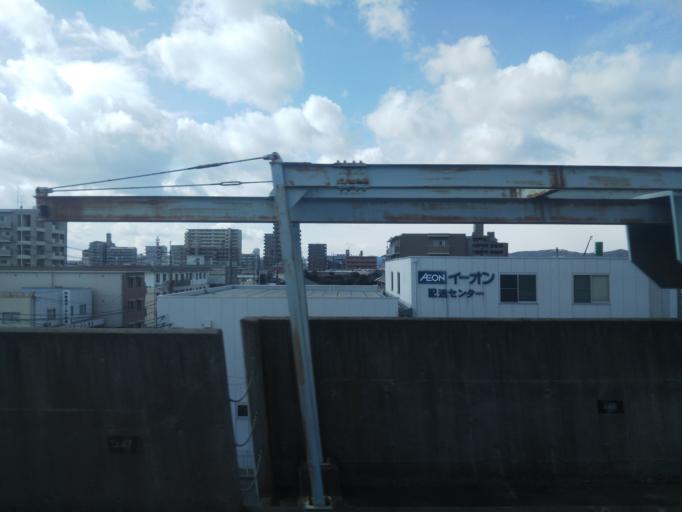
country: JP
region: Okayama
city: Okayama-shi
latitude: 34.6492
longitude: 133.9108
